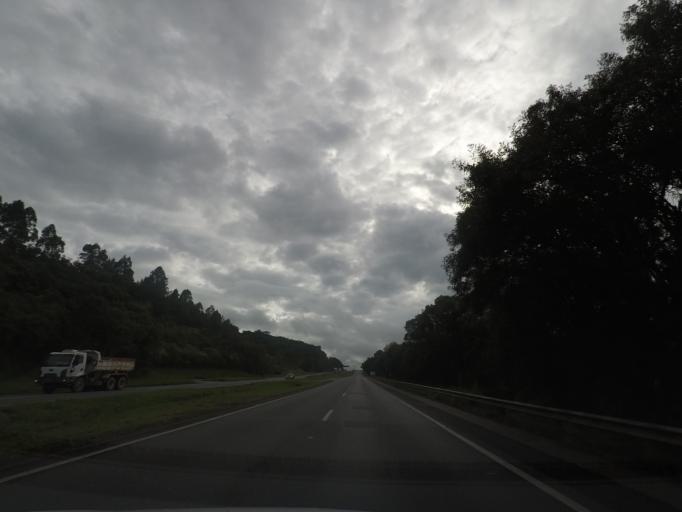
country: BR
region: Parana
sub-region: Campina Grande Do Sul
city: Campina Grande do Sul
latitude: -25.2767
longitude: -48.9238
